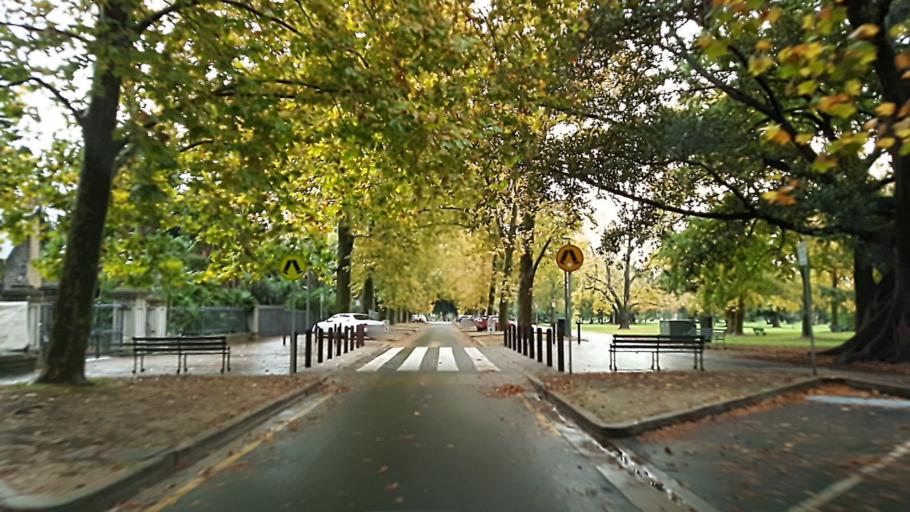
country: AU
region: South Australia
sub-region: Adelaide
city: Adelaide
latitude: -34.9159
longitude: 138.6105
